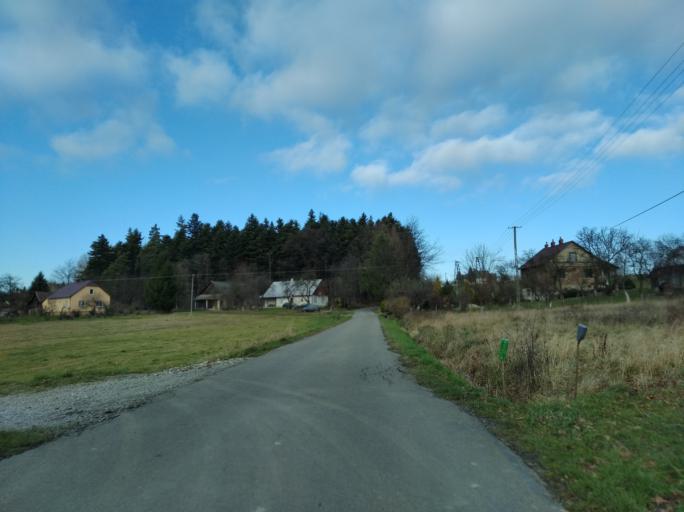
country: PL
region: Subcarpathian Voivodeship
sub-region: Powiat strzyzowski
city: Babica
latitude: 49.9068
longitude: 21.8500
